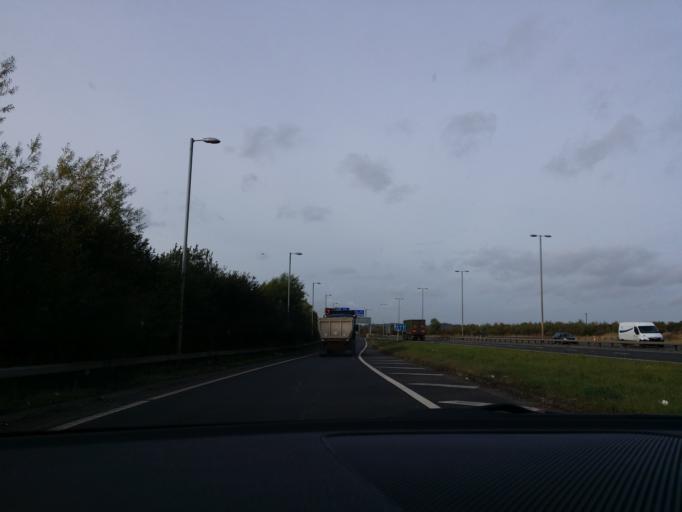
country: GB
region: Scotland
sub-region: Edinburgh
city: Newbridge
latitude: 55.9416
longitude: -3.4038
